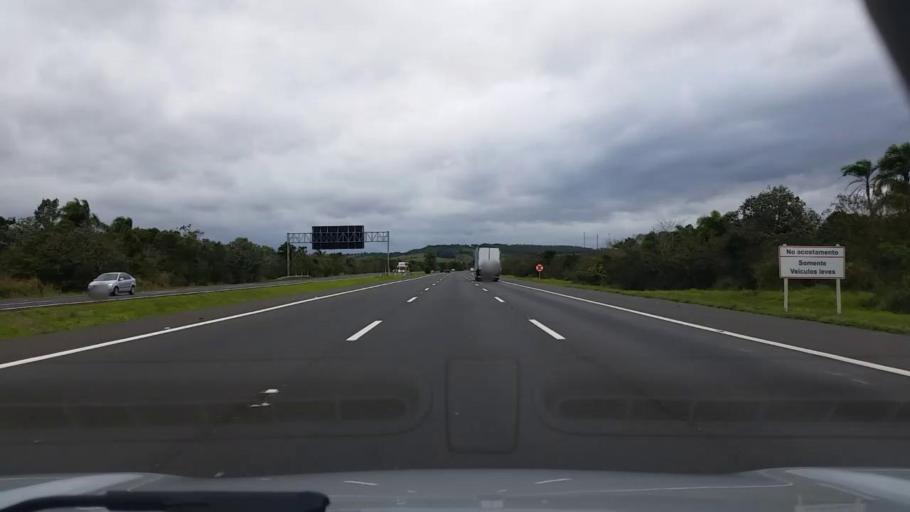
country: BR
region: Rio Grande do Sul
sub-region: Osorio
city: Osorio
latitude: -29.8879
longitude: -50.4560
